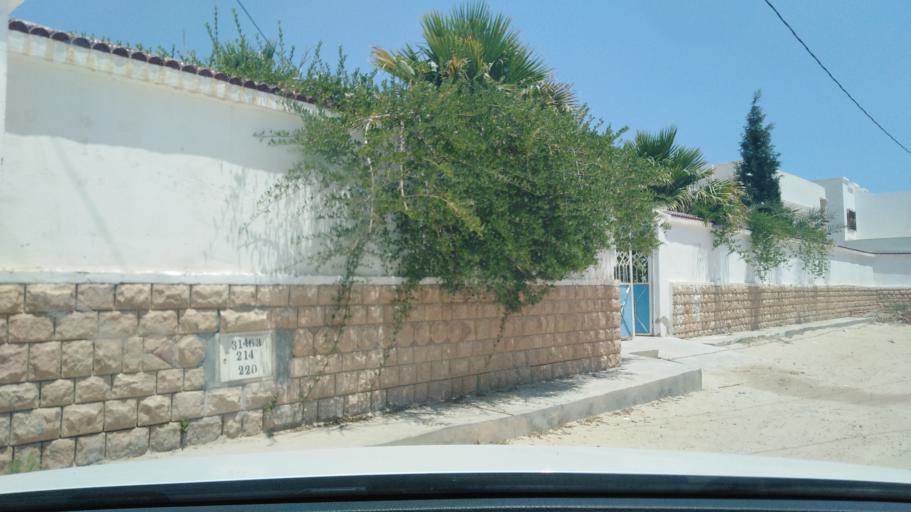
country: TN
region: Qabis
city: Gabes
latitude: 33.9515
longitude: 10.0687
